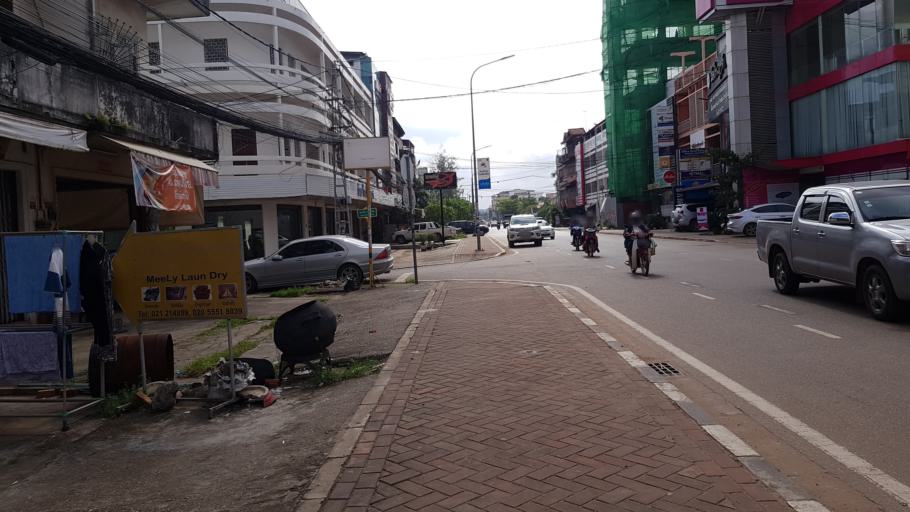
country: LA
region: Vientiane
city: Vientiane
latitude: 17.9678
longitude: 102.6055
